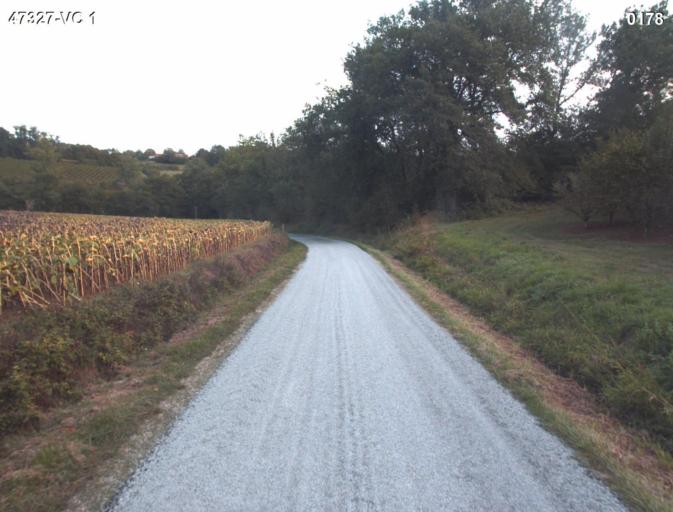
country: FR
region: Aquitaine
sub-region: Departement du Lot-et-Garonne
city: Barbaste
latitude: 44.1875
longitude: 0.2538
